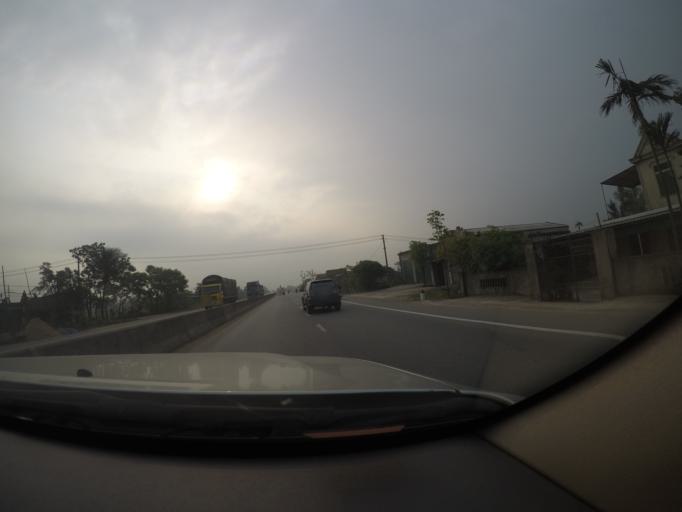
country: VN
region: Ha Tinh
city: Cam Xuyen
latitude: 18.2303
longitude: 106.0383
